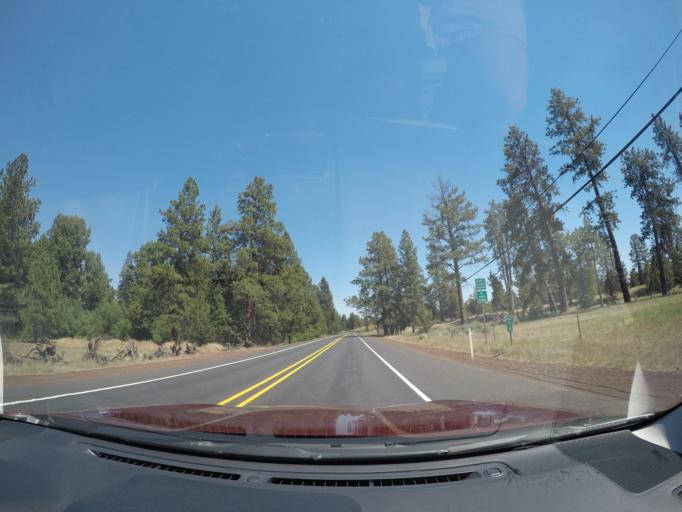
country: US
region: Oregon
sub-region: Deschutes County
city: Sisters
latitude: 44.2873
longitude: -121.5203
